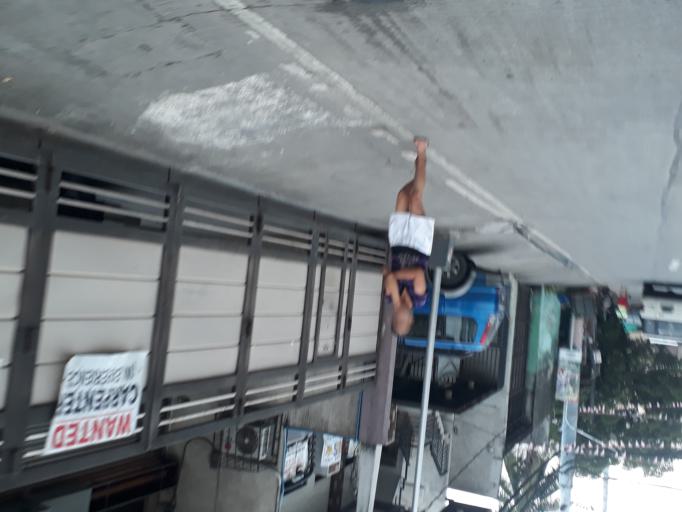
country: PH
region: Metro Manila
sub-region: Caloocan City
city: Niugan
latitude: 14.6661
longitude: 120.9666
